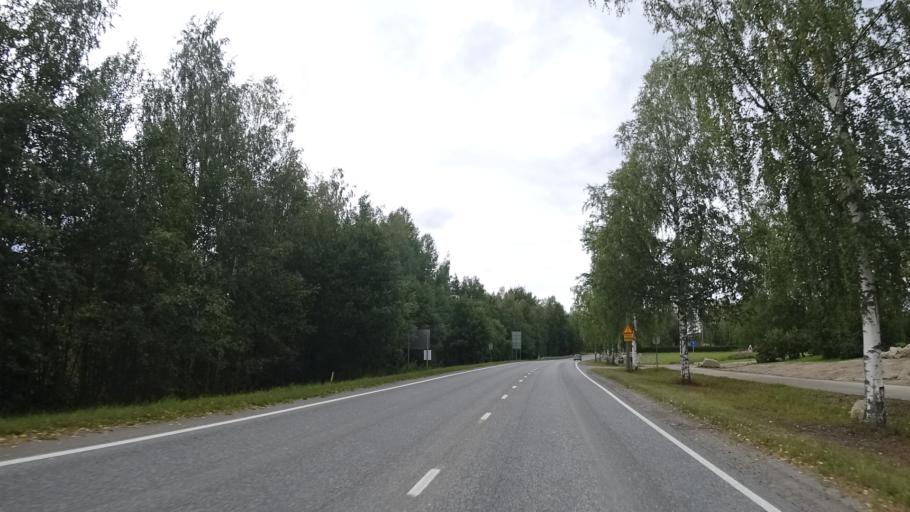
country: FI
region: North Karelia
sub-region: Joensuu
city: Ilomantsi
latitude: 62.6556
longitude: 30.9346
